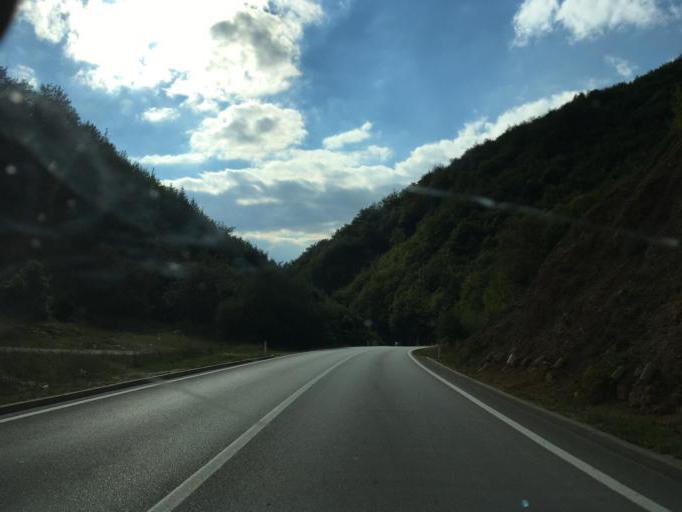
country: BA
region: Federation of Bosnia and Herzegovina
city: Bugojno
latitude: 44.0863
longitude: 17.5393
